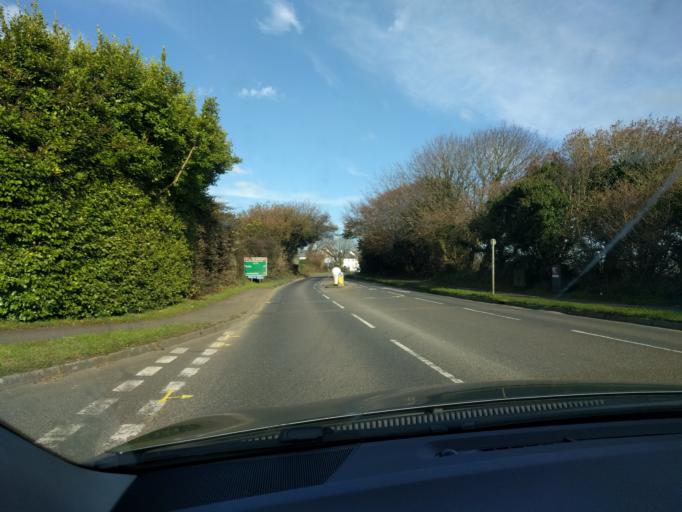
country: GB
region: England
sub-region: Cornwall
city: Camelford
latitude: 50.6138
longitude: -4.6860
